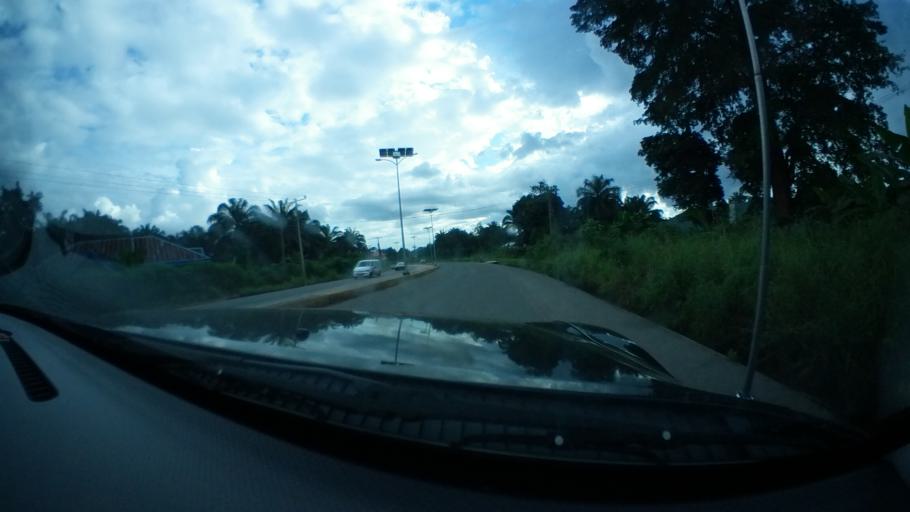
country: NG
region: Imo
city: Orlu
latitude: 5.8298
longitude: 7.0746
